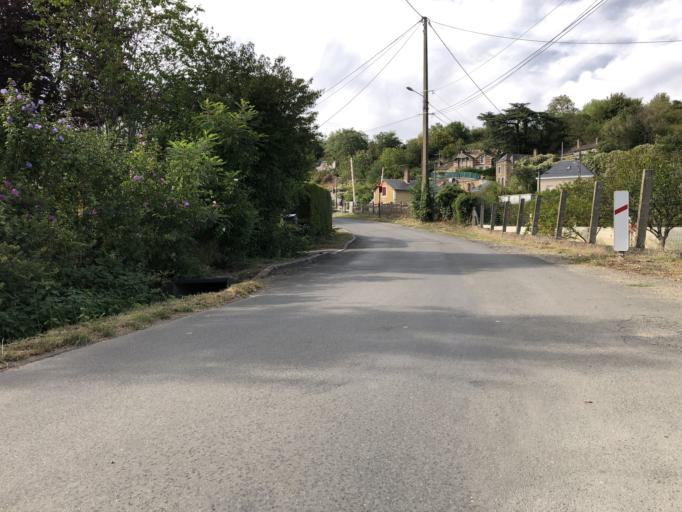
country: FR
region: Pays de la Loire
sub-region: Departement de la Sarthe
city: Chateau-du-Loir
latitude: 47.6819
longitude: 0.4265
